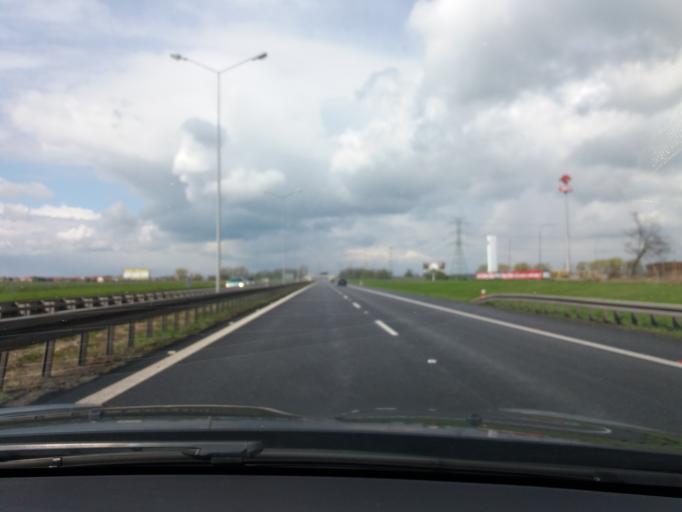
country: PL
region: Lower Silesian Voivodeship
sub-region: Powiat olawski
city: Wierzbno
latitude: 50.8824
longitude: 17.1979
